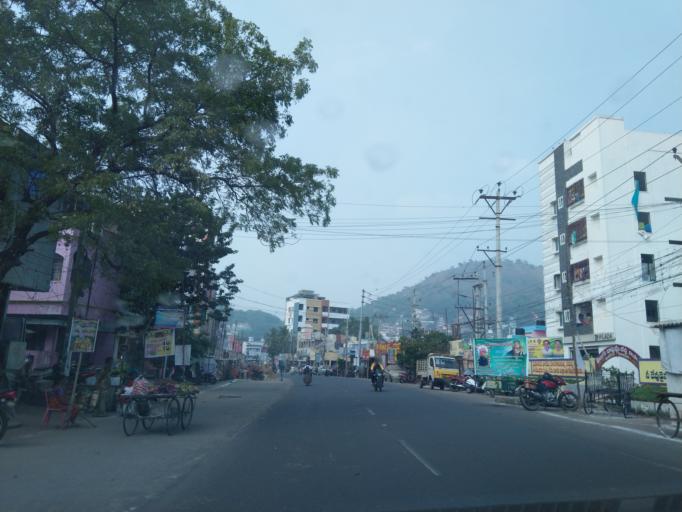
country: IN
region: Andhra Pradesh
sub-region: Krishna
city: Vijayawada
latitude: 16.5305
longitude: 80.6160
